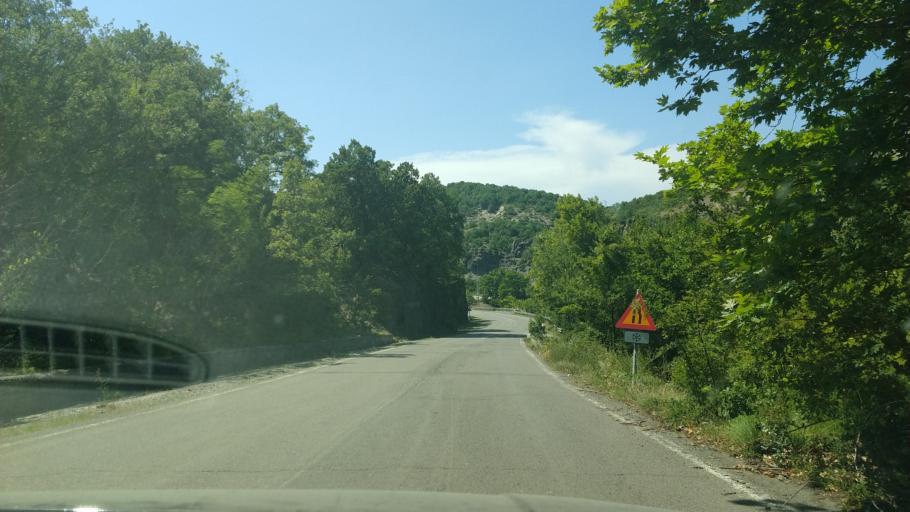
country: GR
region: West Macedonia
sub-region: Nomos Grevenon
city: Grevena
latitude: 40.0498
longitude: 21.4834
